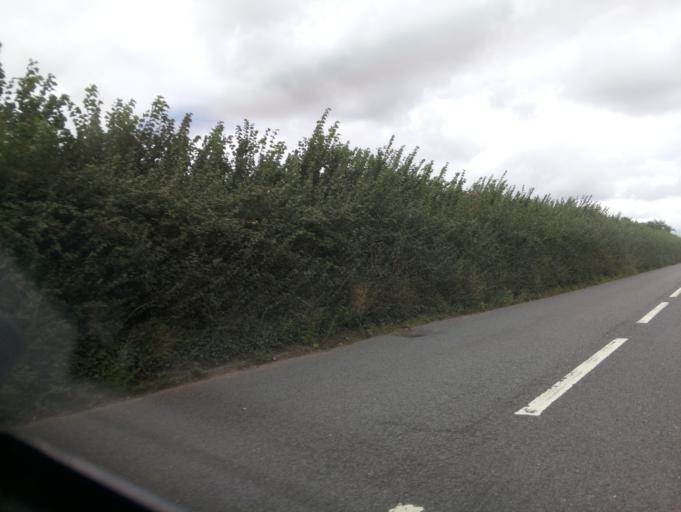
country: GB
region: England
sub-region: Devon
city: Heavitree
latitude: 50.7594
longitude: -3.4421
